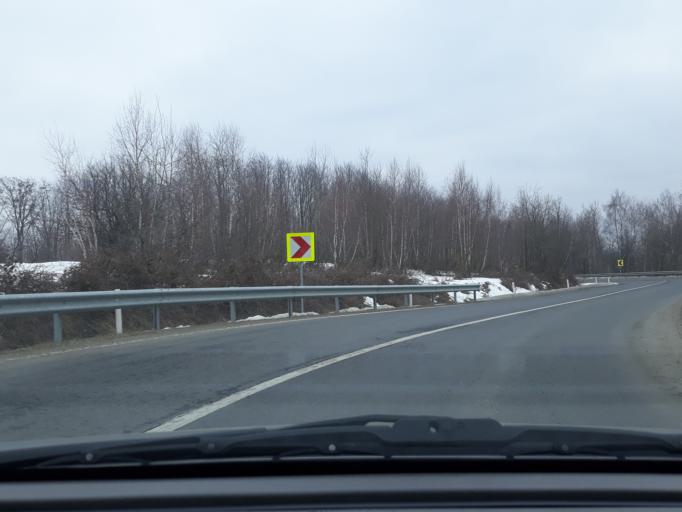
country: RO
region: Bihor
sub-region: Oras Alesd
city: Padurea Neagra
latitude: 47.1211
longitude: 22.4340
